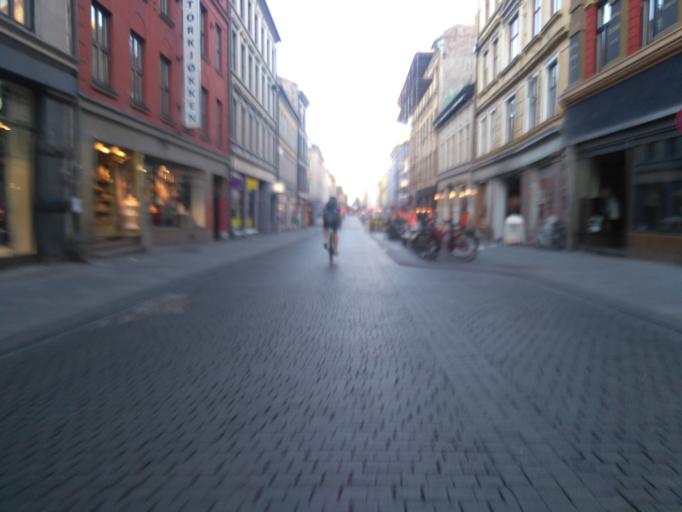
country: NO
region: Oslo
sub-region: Oslo
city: Oslo
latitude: 59.9174
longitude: 10.7540
